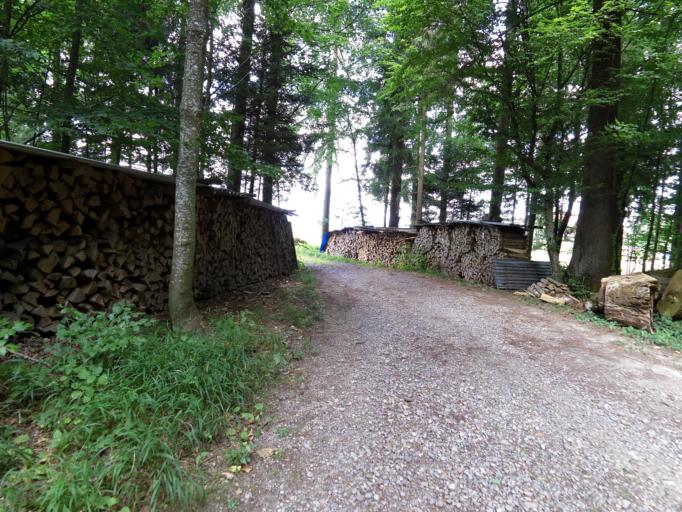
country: CH
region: Thurgau
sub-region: Kreuzlingen District
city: Tagerwilen
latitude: 47.6504
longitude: 9.1106
